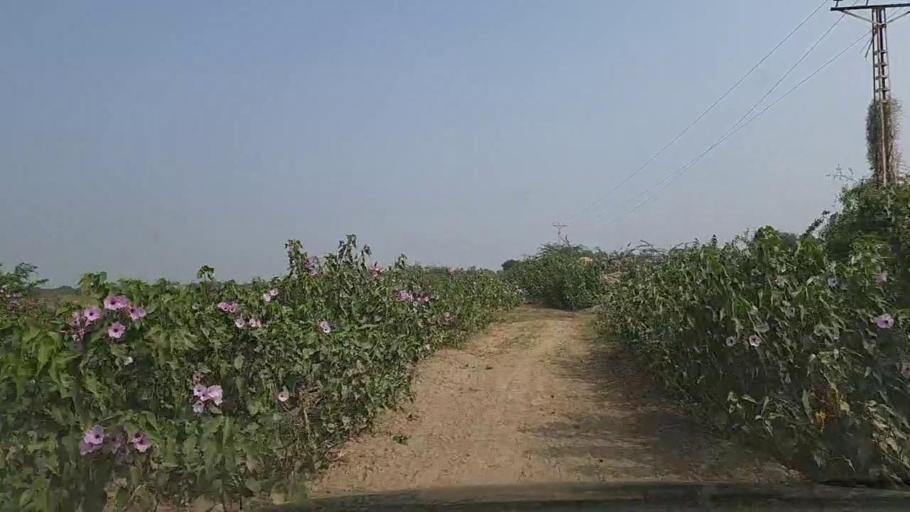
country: PK
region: Sindh
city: Thatta
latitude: 24.7610
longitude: 67.8046
